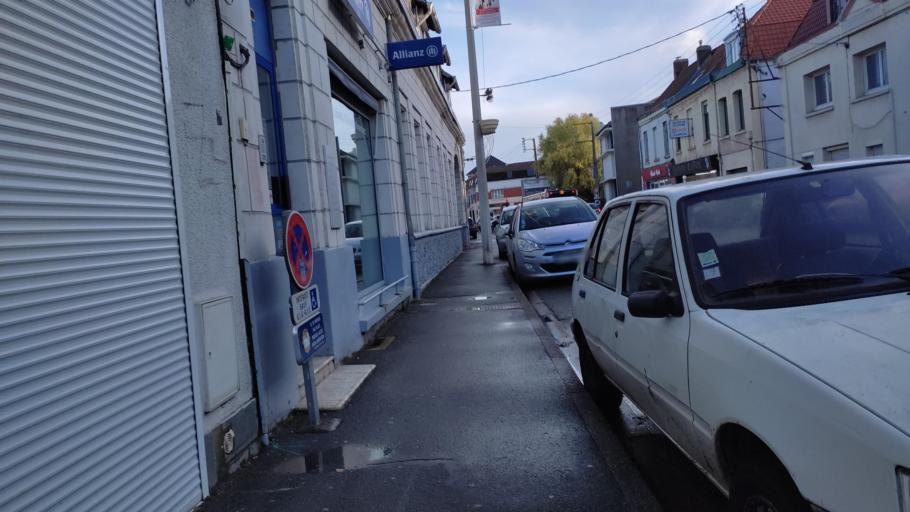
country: FR
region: Nord-Pas-de-Calais
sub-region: Departement du Pas-de-Calais
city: Bethune
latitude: 50.5265
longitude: 2.6473
